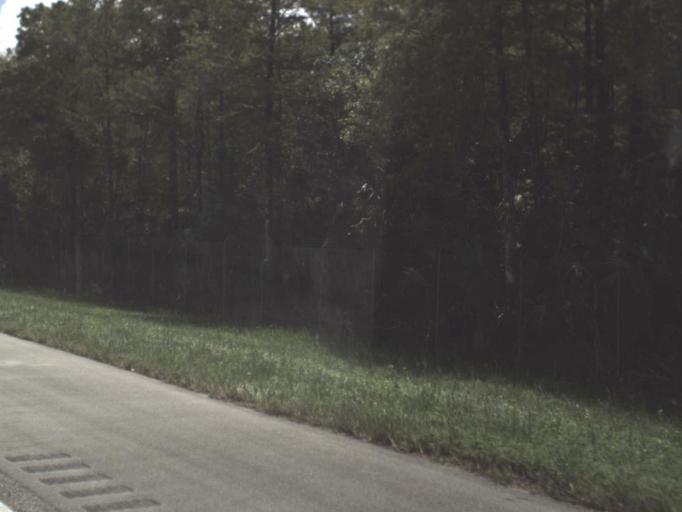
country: US
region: Florida
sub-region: Collier County
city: Orangetree
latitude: 26.1536
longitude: -81.4043
